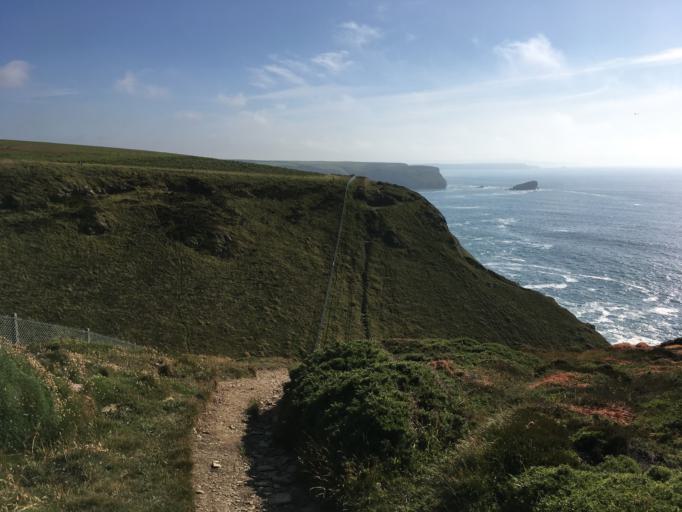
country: GB
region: England
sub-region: Cornwall
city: Camborne
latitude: 50.2710
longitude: -5.2791
